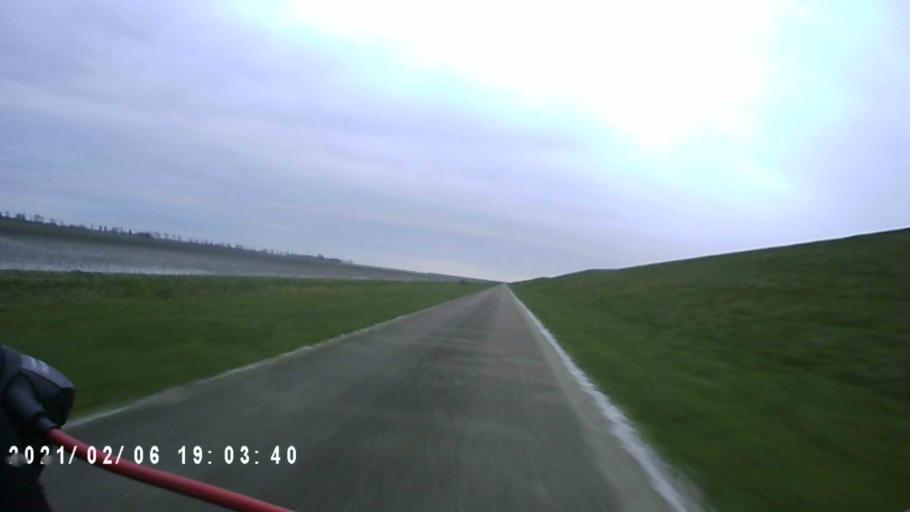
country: NL
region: Groningen
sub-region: Gemeente Winsum
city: Winsum
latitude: 53.4228
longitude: 6.4754
